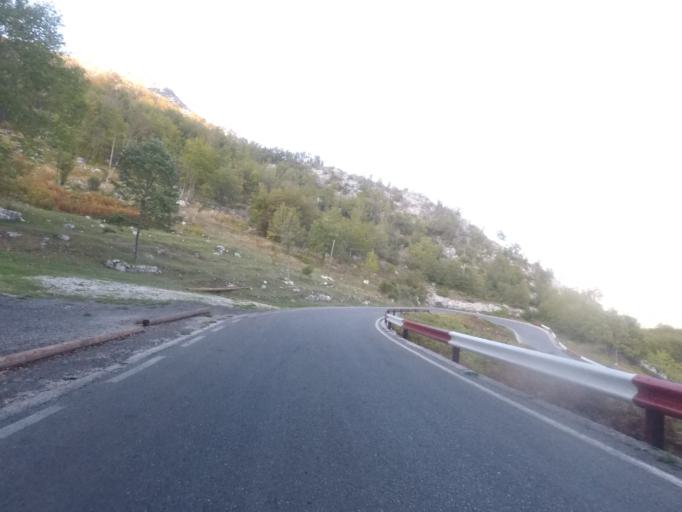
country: ME
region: Cetinje
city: Cetinje
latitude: 42.3674
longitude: 18.8864
